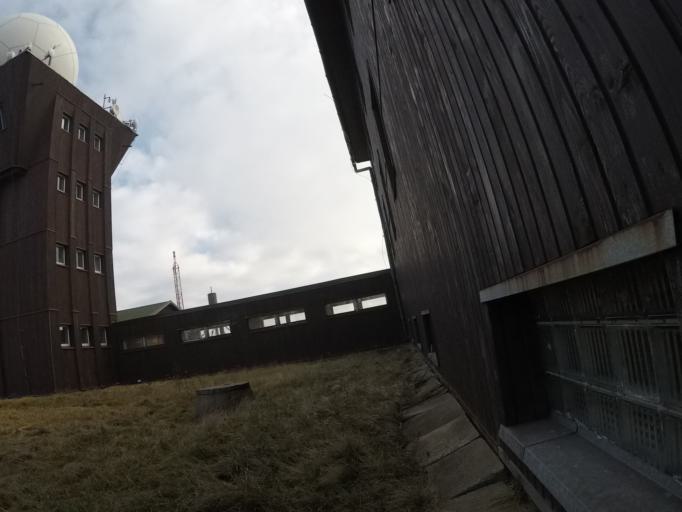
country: SK
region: Kosicky
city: Gelnica
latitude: 48.7828
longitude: 20.9870
